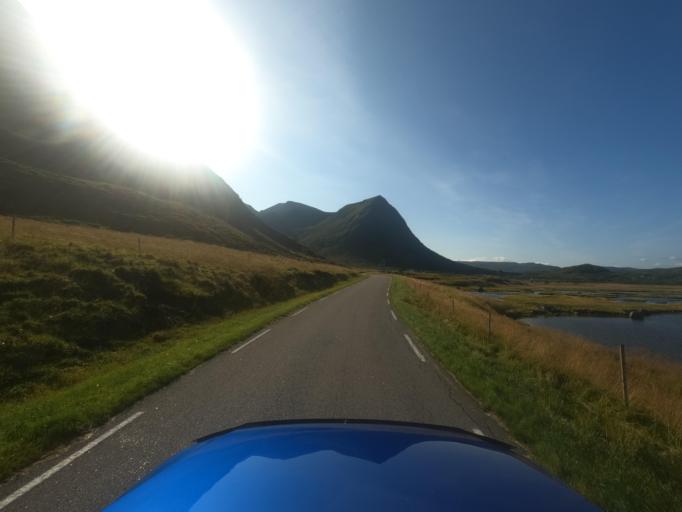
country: NO
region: Nordland
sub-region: Vestvagoy
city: Evjen
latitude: 68.3289
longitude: 13.9192
